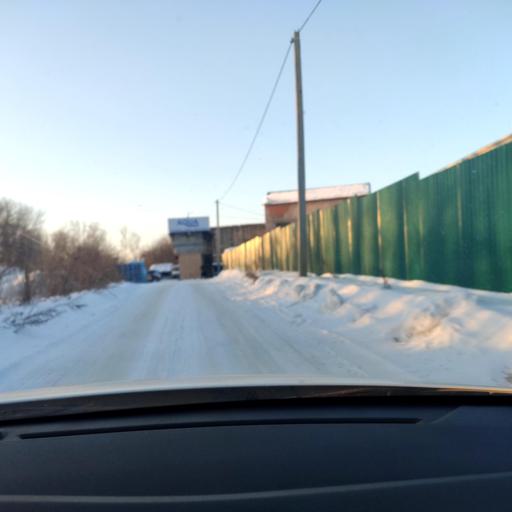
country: RU
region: Bashkortostan
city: Avdon
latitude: 54.6823
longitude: 55.8123
